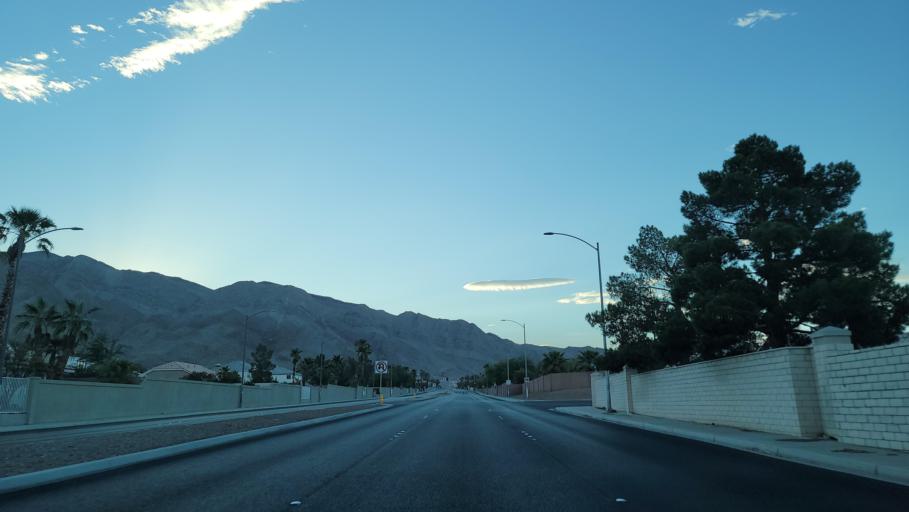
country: US
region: Nevada
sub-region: Clark County
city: Sunrise Manor
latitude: 36.1593
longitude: -115.0301
